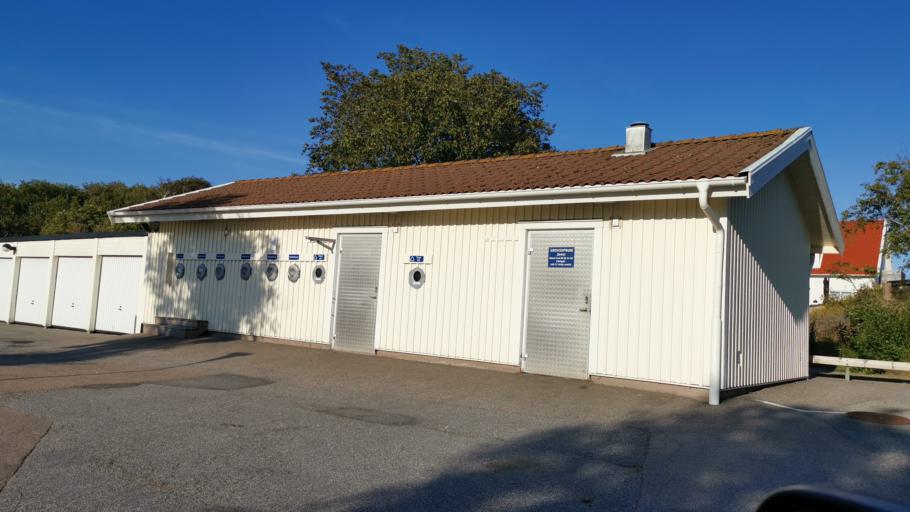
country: SE
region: Vaestra Goetaland
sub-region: Lysekils Kommun
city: Lysekil
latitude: 58.2794
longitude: 11.4329
